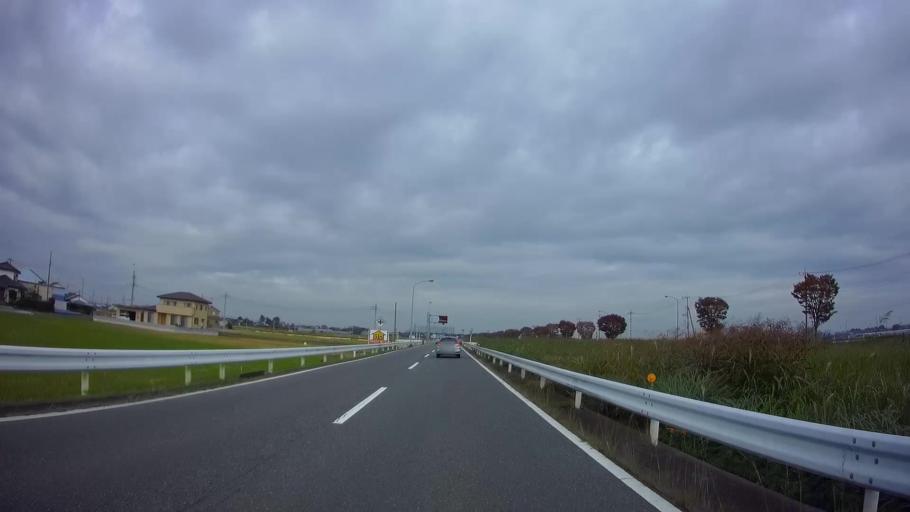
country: JP
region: Saitama
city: Gyoda
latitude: 36.1426
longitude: 139.4281
